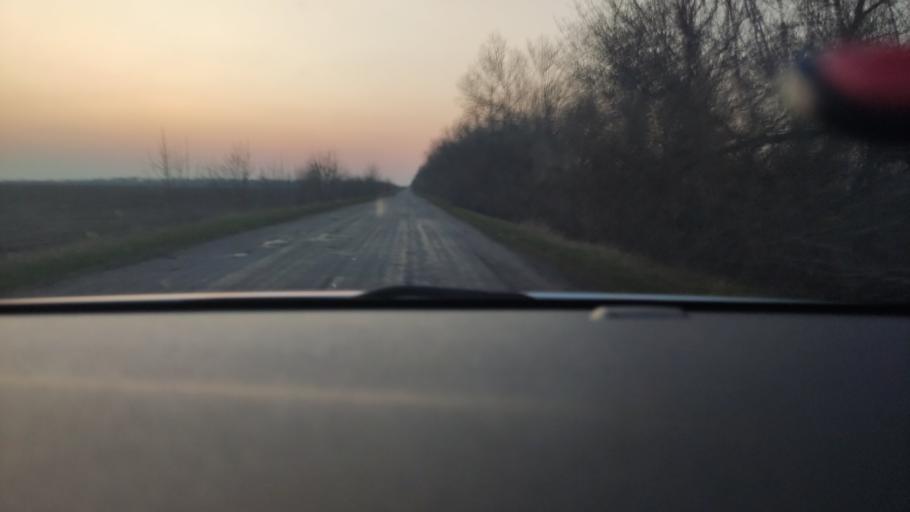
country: RU
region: Voronezj
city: Uryv-Pokrovka
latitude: 51.1422
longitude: 39.0723
